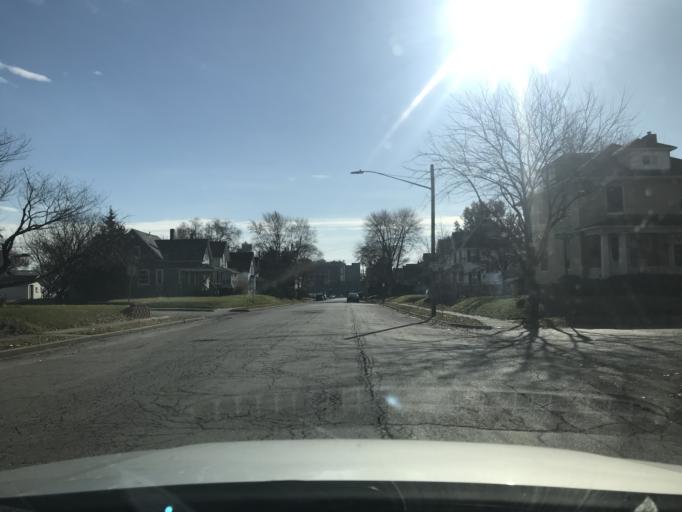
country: US
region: Iowa
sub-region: Scott County
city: Davenport
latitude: 41.5194
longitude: -90.6094
